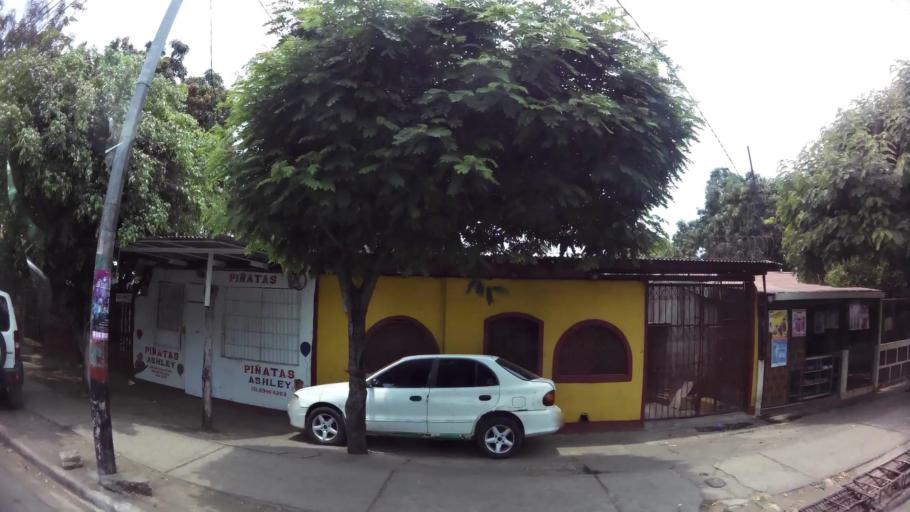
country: NI
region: Managua
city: Managua
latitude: 12.1184
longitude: -86.2393
